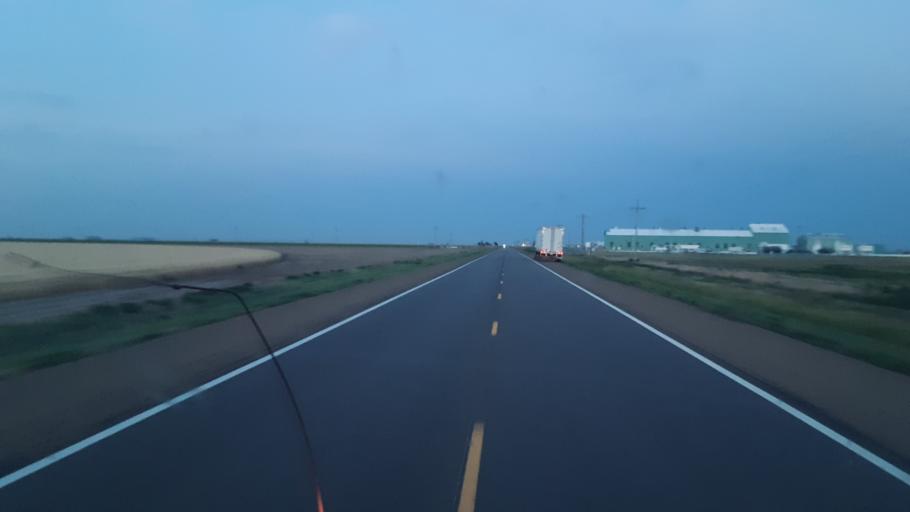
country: US
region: Kansas
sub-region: Finney County
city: Holcomb
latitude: 38.0034
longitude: -101.0531
